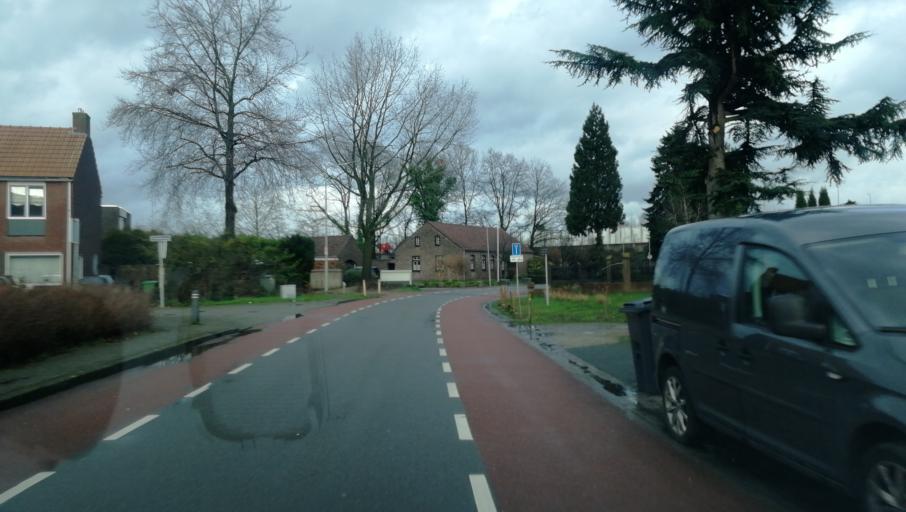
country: NL
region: Limburg
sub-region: Gemeente Venlo
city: Tegelen
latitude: 51.3475
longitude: 6.1549
